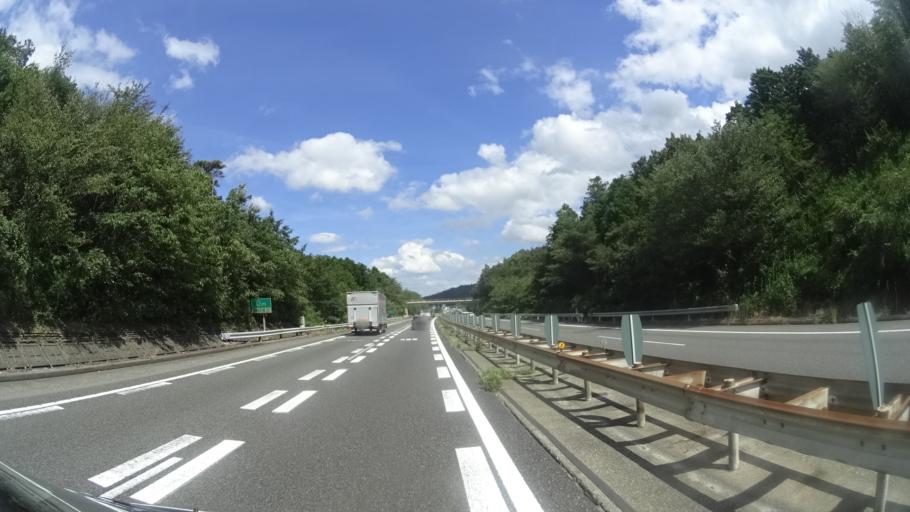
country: JP
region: Shiga Prefecture
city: Youkaichi
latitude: 35.1464
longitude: 136.2802
